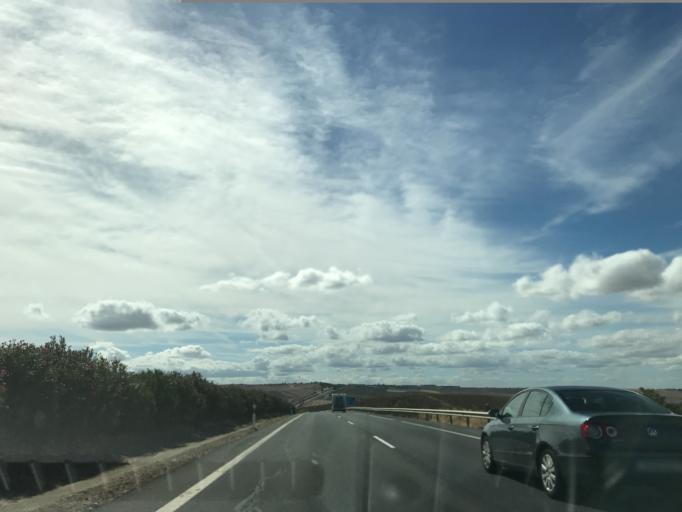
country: ES
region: Andalusia
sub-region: Province of Cordoba
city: La Victoria
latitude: 37.7453
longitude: -4.8482
